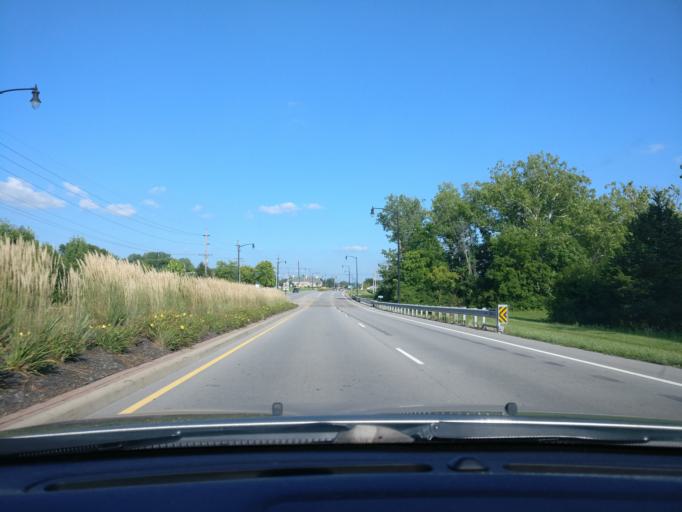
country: US
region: Ohio
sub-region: Warren County
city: Springboro
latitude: 39.5611
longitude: -84.2494
